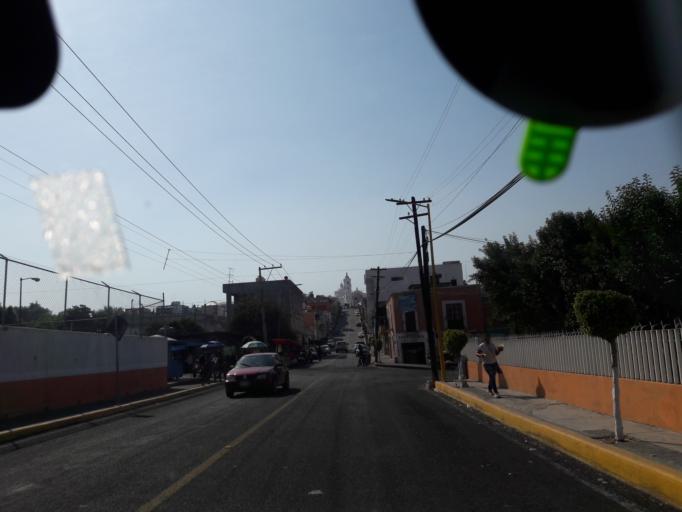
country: MX
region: Tlaxcala
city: Panotla
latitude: 19.3169
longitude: -98.2696
